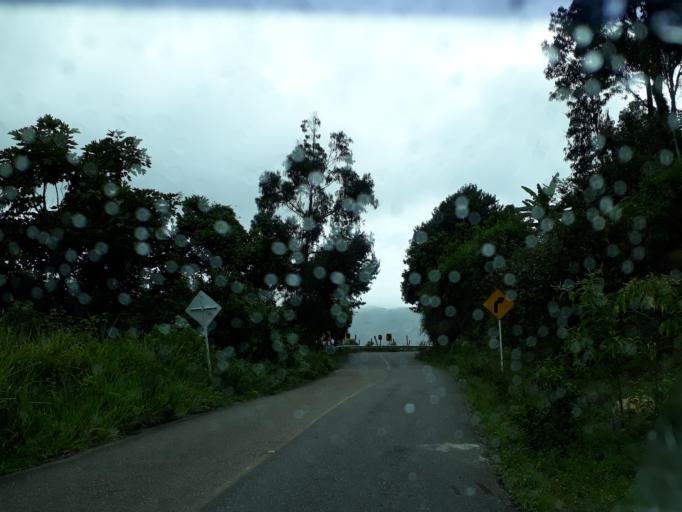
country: CO
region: Cundinamarca
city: Cabrera
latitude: 4.0138
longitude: -74.5078
